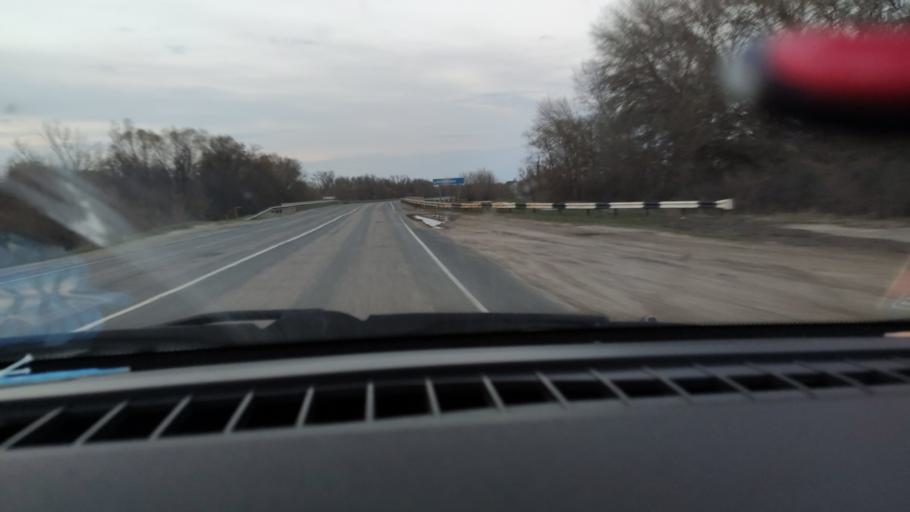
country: RU
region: Saratov
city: Sinodskoye
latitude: 51.9790
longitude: 46.6530
